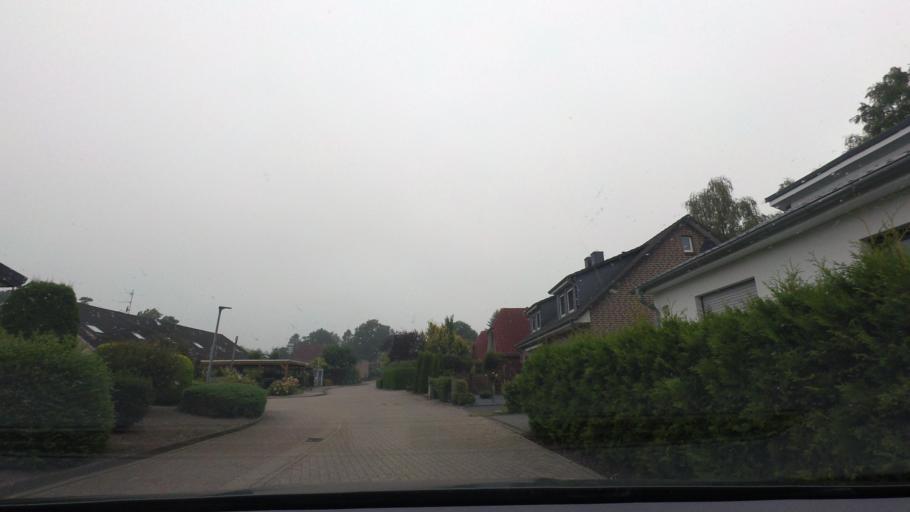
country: DE
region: Lower Saxony
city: Hude
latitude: 53.0991
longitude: 8.4804
